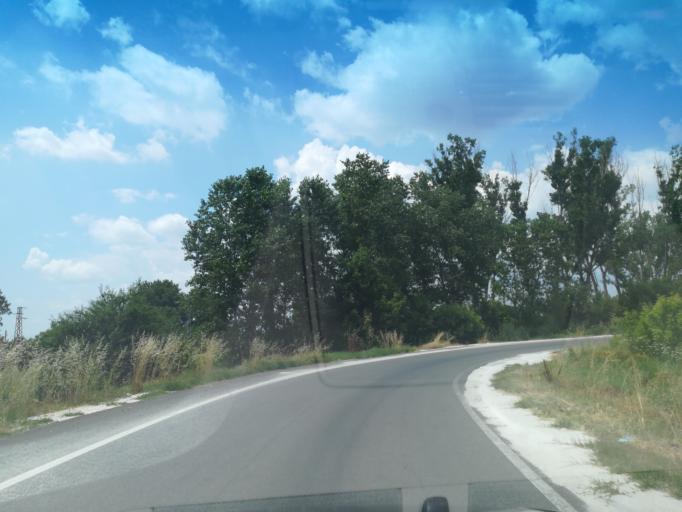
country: BG
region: Plovdiv
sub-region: Obshtina Plovdiv
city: Plovdiv
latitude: 42.2023
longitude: 24.6670
